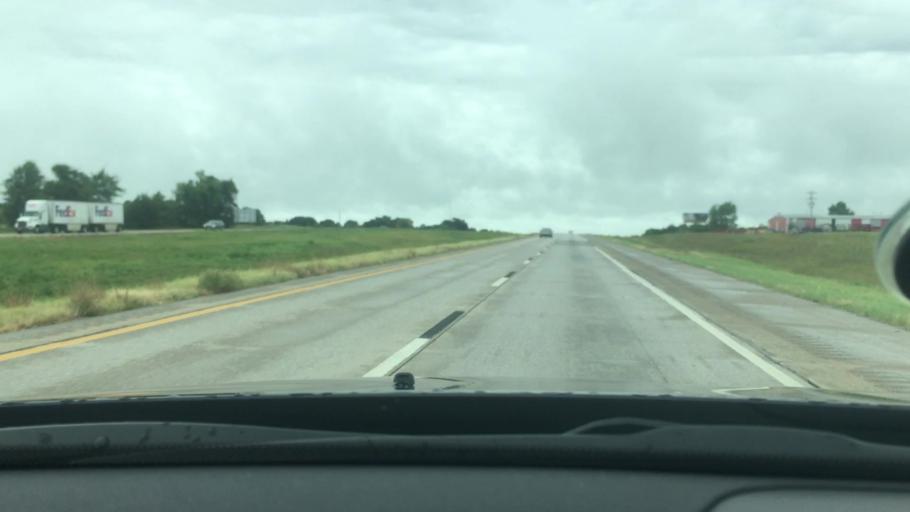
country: US
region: Oklahoma
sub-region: Atoka County
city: Atoka
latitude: 34.1994
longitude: -96.2393
